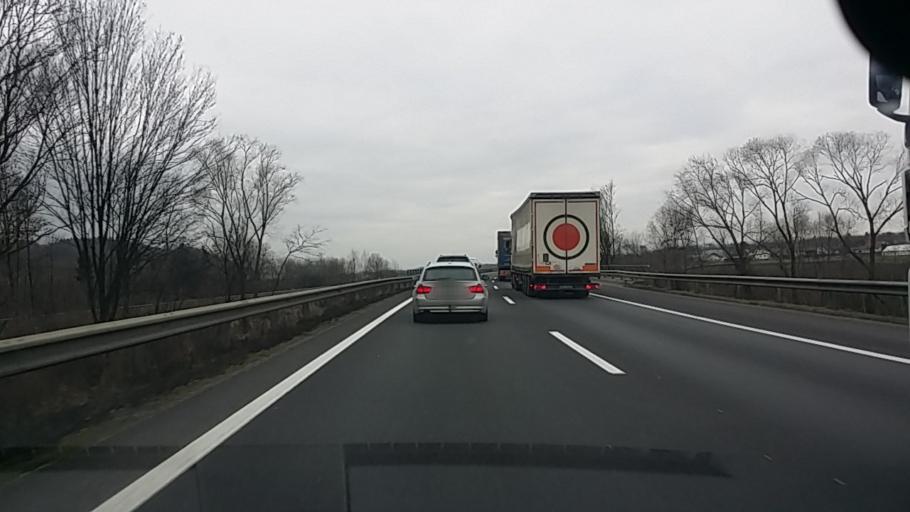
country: AT
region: Upper Austria
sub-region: Politischer Bezirk Linz-Land
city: Traun
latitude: 48.1926
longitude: 14.2299
